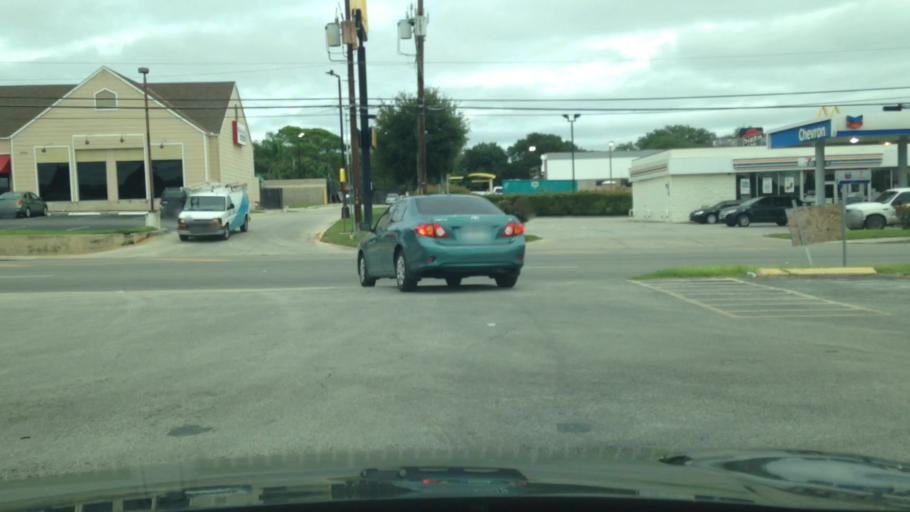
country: US
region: Texas
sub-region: Bexar County
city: Hollywood Park
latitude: 29.5785
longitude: -98.4426
